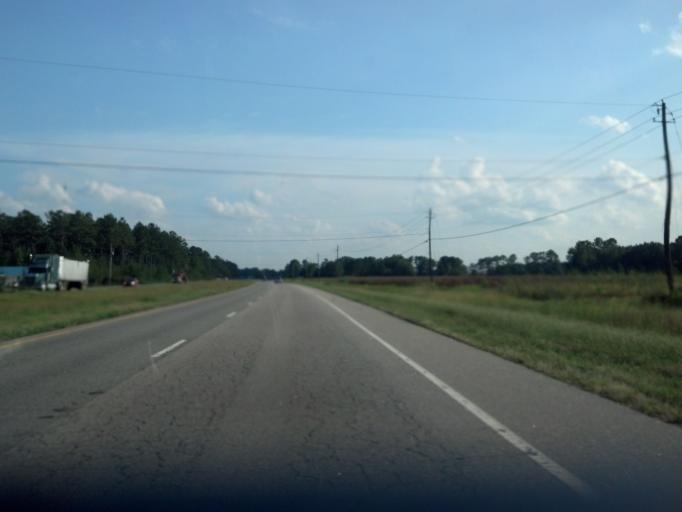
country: US
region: North Carolina
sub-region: Pitt County
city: Greenville
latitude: 35.6876
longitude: -77.3663
